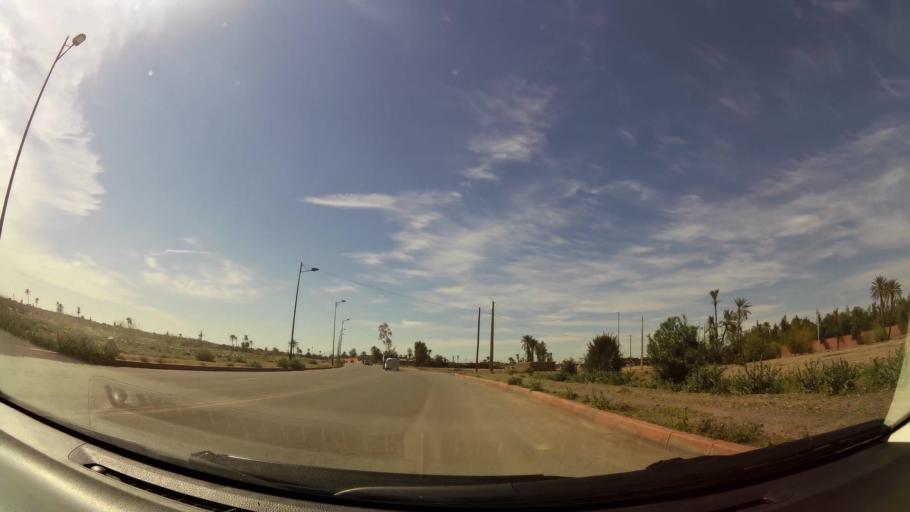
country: MA
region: Marrakech-Tensift-Al Haouz
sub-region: Marrakech
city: Marrakesh
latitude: 31.6182
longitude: -7.9573
